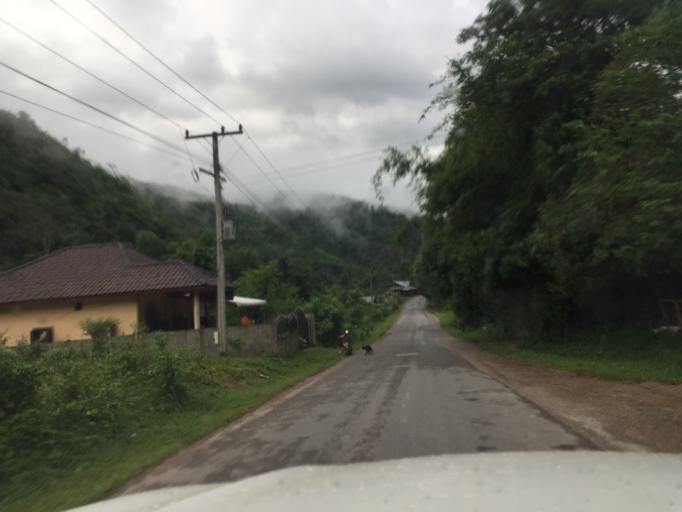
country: LA
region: Oudomxai
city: Muang La
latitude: 20.8739
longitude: 102.1344
